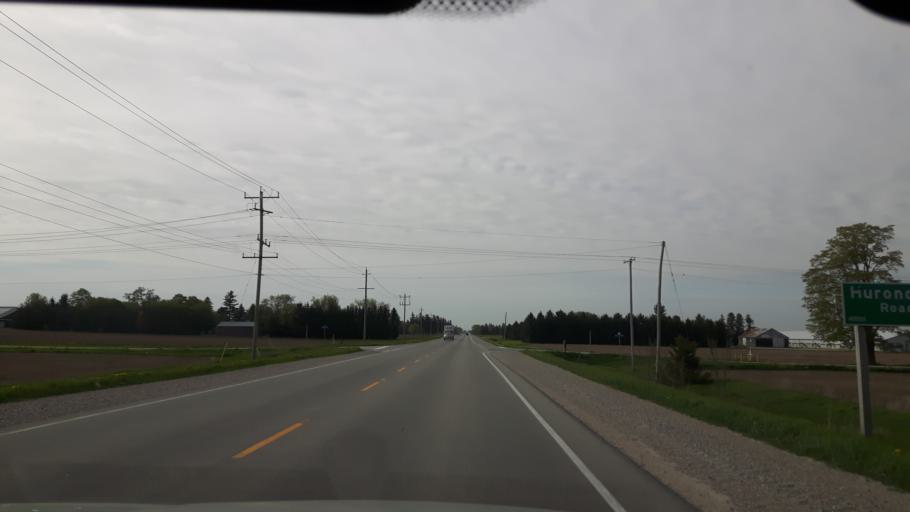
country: CA
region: Ontario
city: South Huron
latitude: 43.3989
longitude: -81.4913
